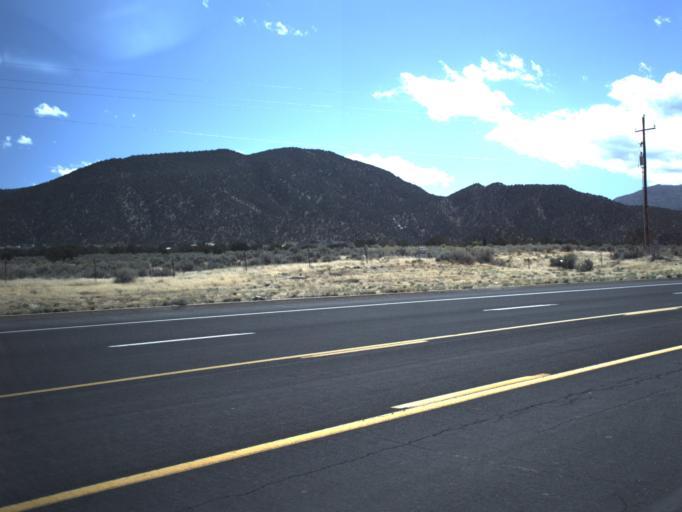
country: US
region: Utah
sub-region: Iron County
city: Cedar City
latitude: 37.7242
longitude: -113.0500
